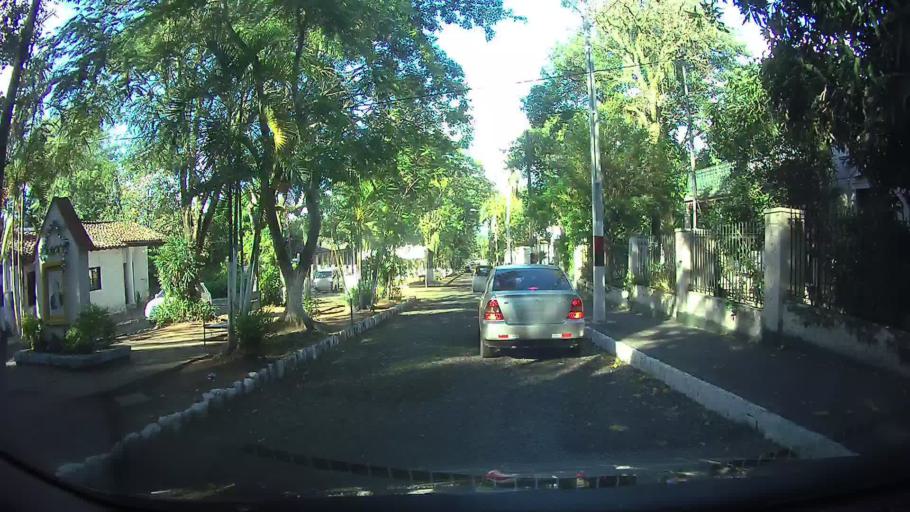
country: PY
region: Central
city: Aregua
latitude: -25.3116
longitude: -57.3844
